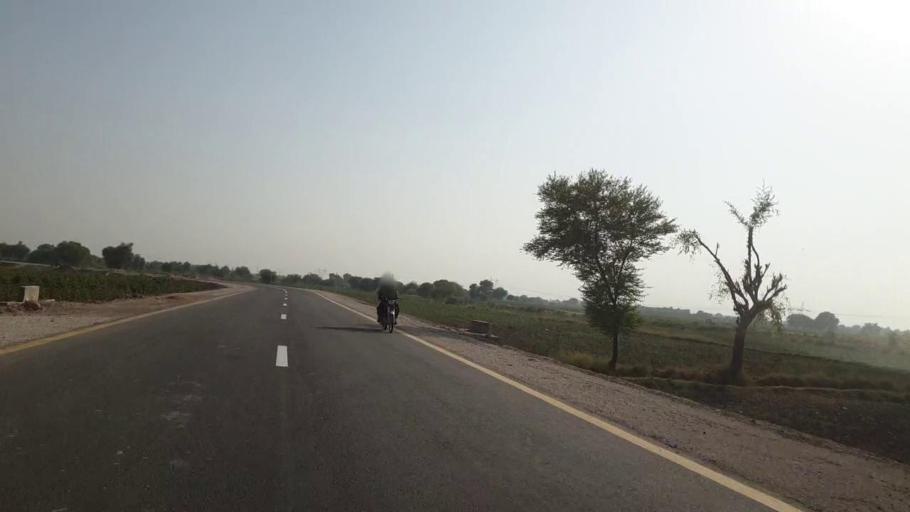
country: PK
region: Sindh
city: Bhan
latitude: 26.4846
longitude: 67.7795
